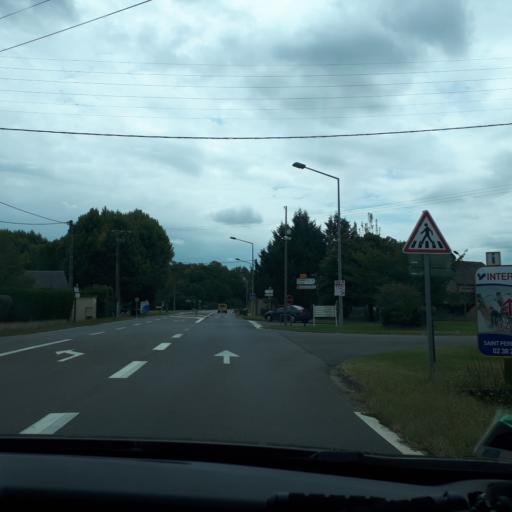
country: FR
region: Centre
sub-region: Departement du Loiret
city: Saint-Pere-sur-Loire
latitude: 47.7976
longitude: 2.3815
